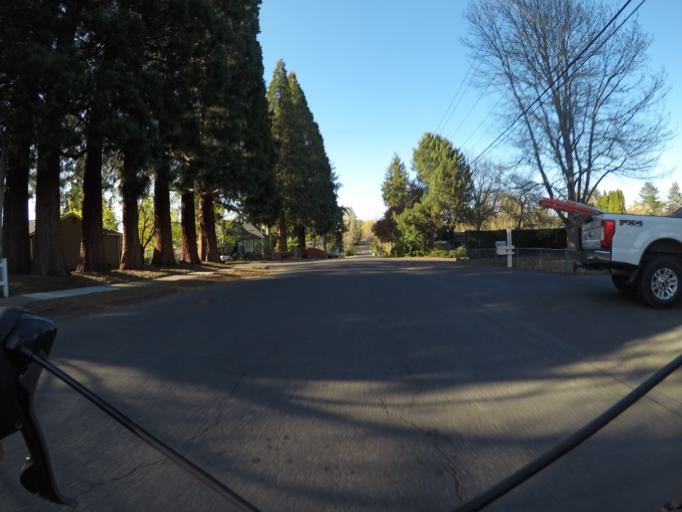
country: US
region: Oregon
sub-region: Washington County
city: Aloha
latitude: 45.4825
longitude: -122.8751
